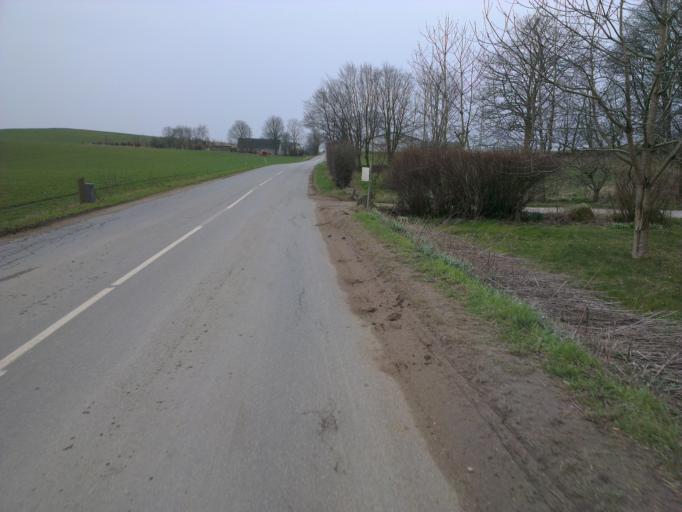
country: DK
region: Capital Region
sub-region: Frederikssund Kommune
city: Skibby
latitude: 55.7449
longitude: 11.9271
